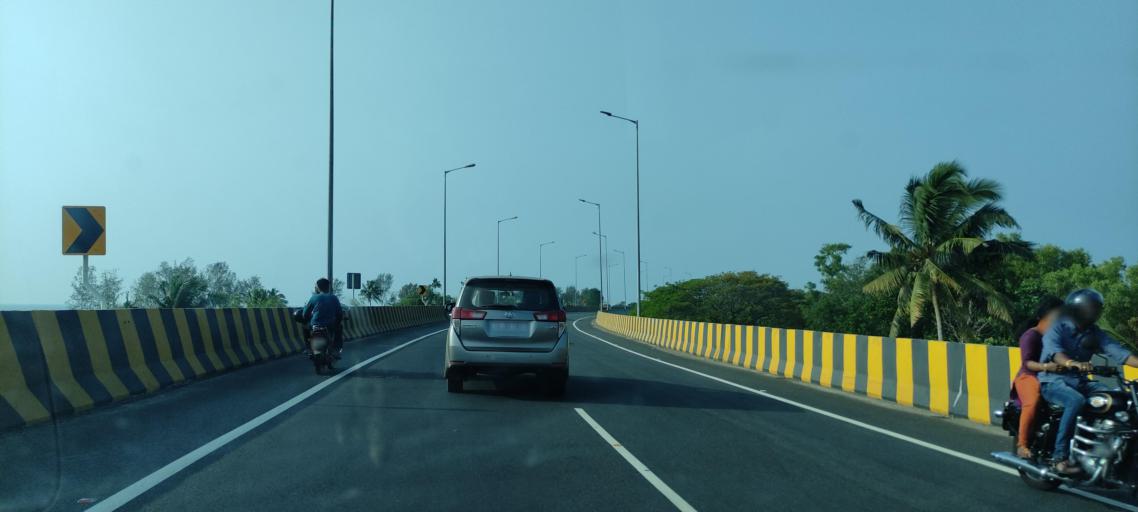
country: IN
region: Kerala
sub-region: Alappuzha
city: Alleppey
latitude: 9.4784
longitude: 76.3226
